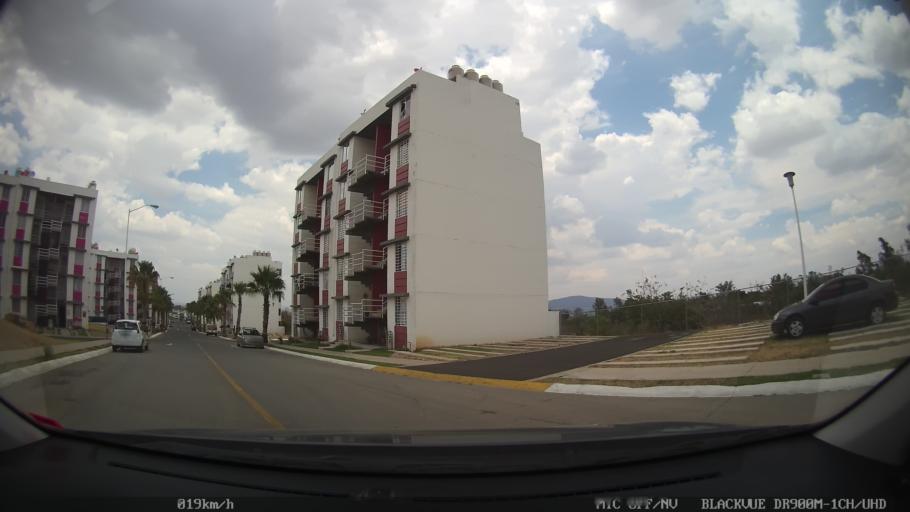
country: MX
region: Jalisco
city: Tonala
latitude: 20.6388
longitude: -103.2248
